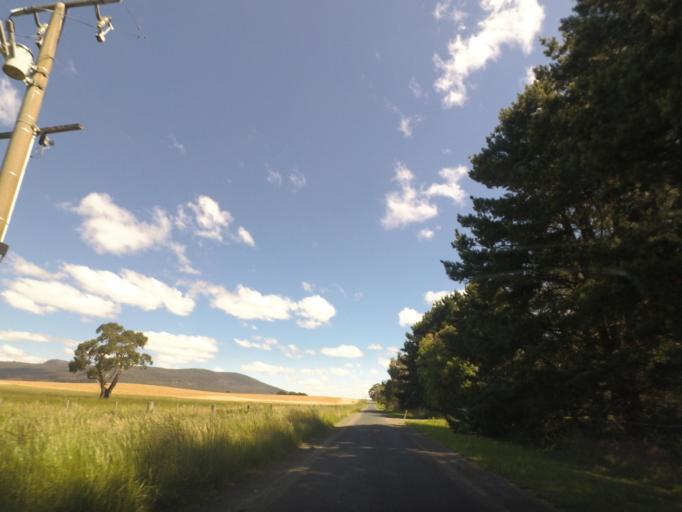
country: AU
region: Victoria
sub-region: Hume
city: Sunbury
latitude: -37.3274
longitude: 144.5598
